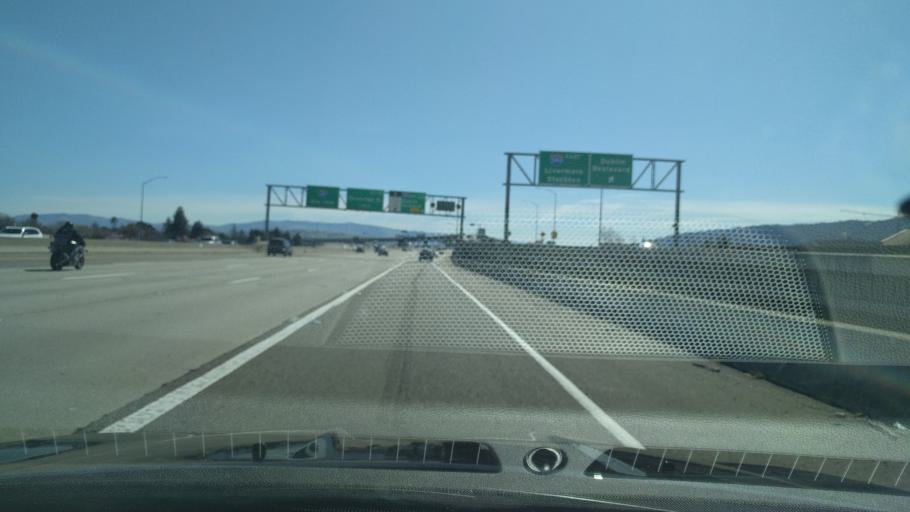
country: US
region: California
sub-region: Alameda County
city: Dublin
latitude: 37.7070
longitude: -121.9268
